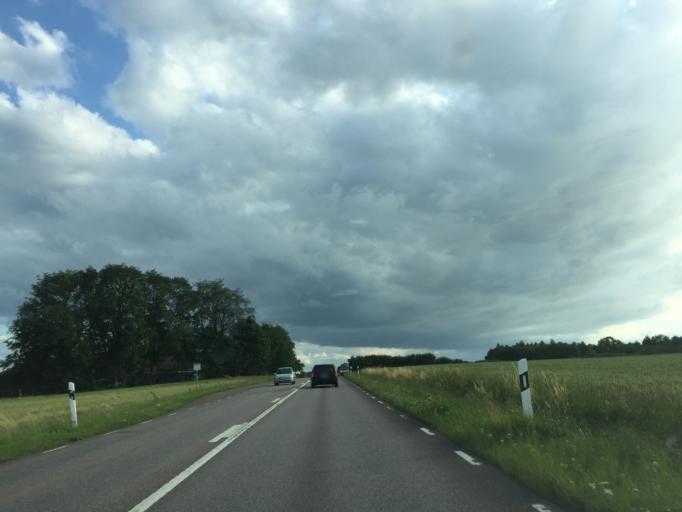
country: SE
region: OEstergoetland
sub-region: Motala Kommun
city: Motala
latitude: 58.5015
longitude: 15.0132
